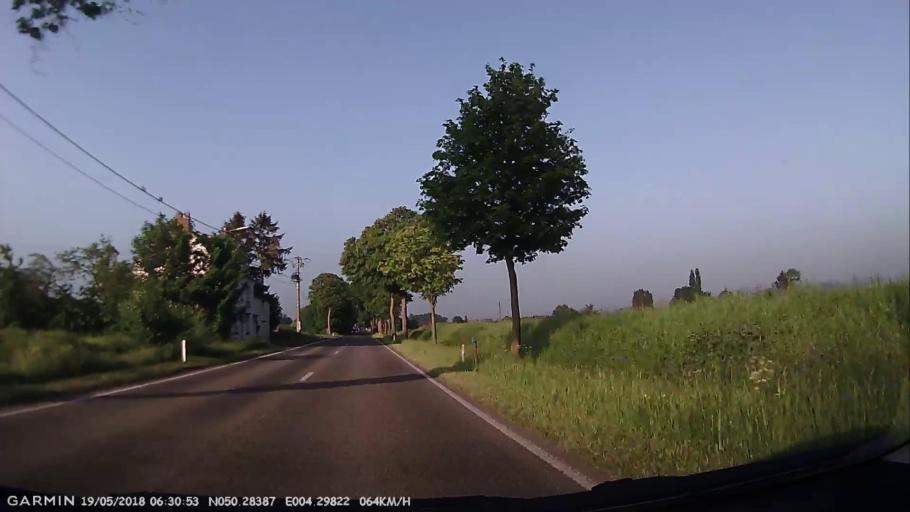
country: BE
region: Wallonia
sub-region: Province du Hainaut
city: Thuin
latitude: 50.2839
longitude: 4.2982
